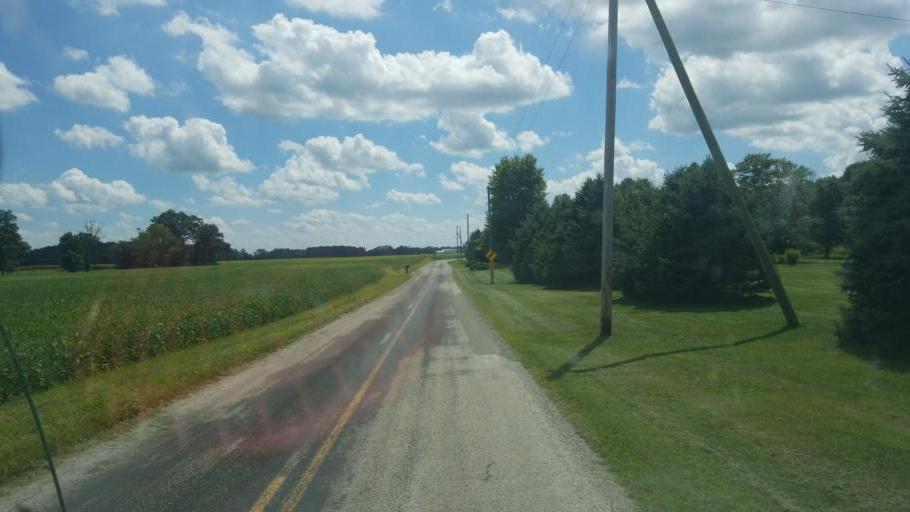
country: US
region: Ohio
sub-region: Marion County
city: Prospect
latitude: 40.4719
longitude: -83.1668
